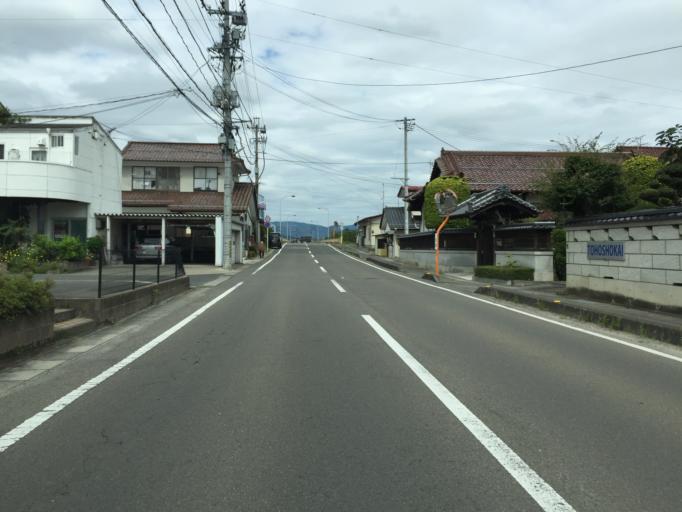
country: JP
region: Fukushima
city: Hobaramachi
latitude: 37.8090
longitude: 140.4944
